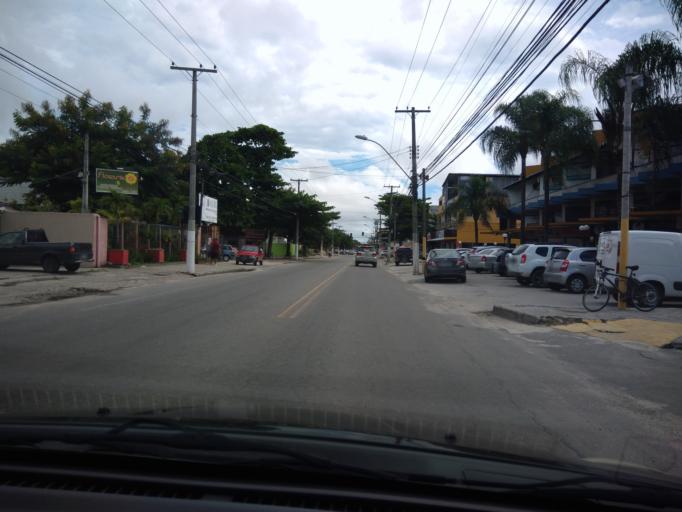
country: BR
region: Rio de Janeiro
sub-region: Niteroi
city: Niteroi
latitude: -22.9416
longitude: -43.0287
